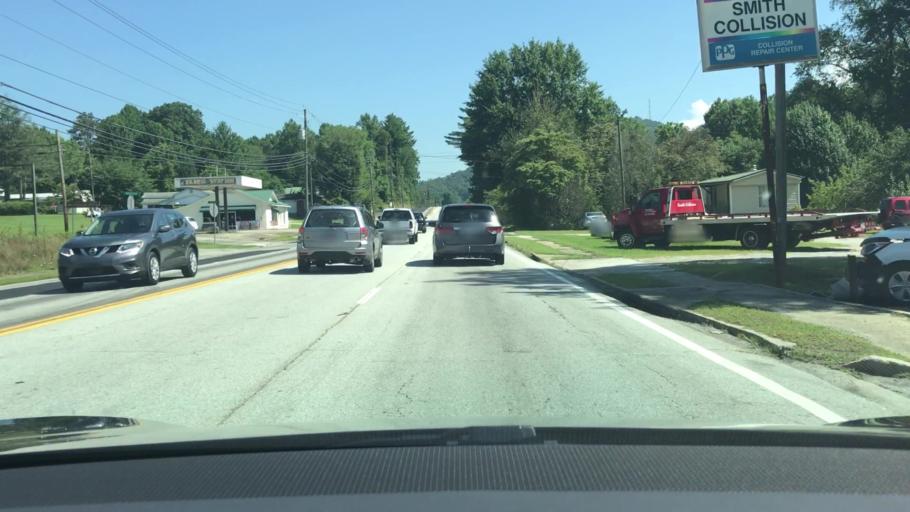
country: US
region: Georgia
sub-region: Rabun County
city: Mountain City
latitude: 34.9122
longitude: -83.3872
